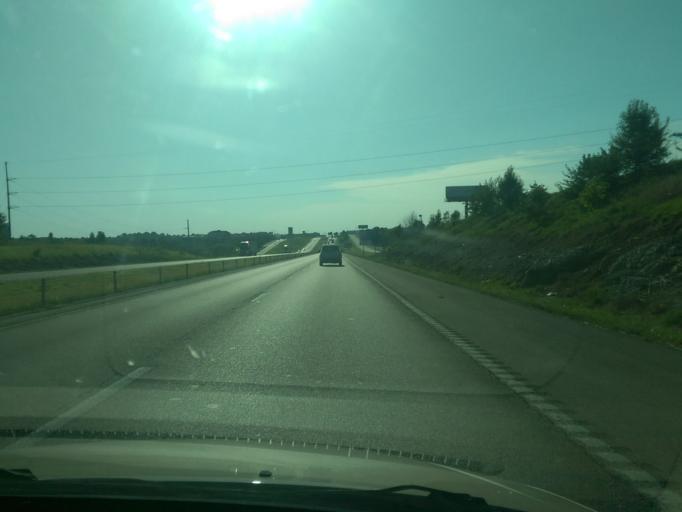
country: US
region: Missouri
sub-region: Jackson County
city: Grain Valley
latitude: 39.0257
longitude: -94.2327
